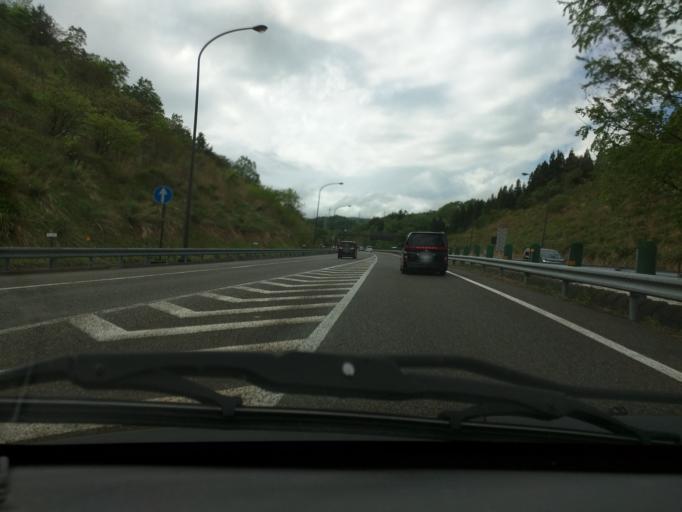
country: JP
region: Niigata
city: Joetsu
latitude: 37.1377
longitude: 138.2143
